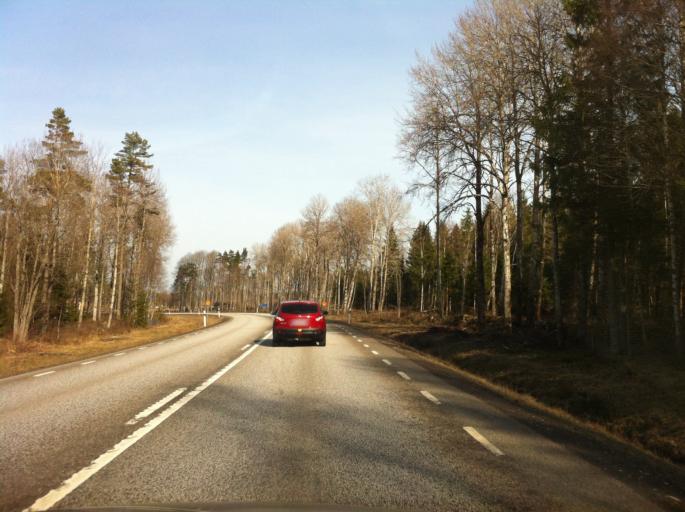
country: SE
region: Joenkoeping
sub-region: Mullsjo Kommun
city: Mullsjoe
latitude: 58.0299
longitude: 13.8369
